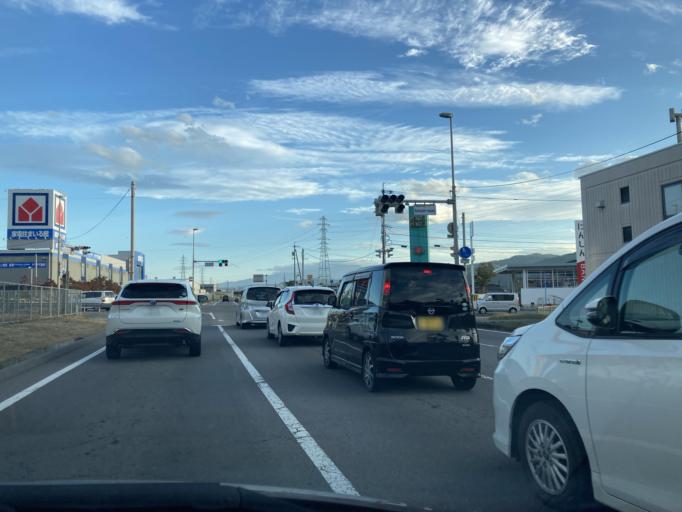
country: JP
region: Nagano
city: Ueda
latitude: 36.4025
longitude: 138.2735
